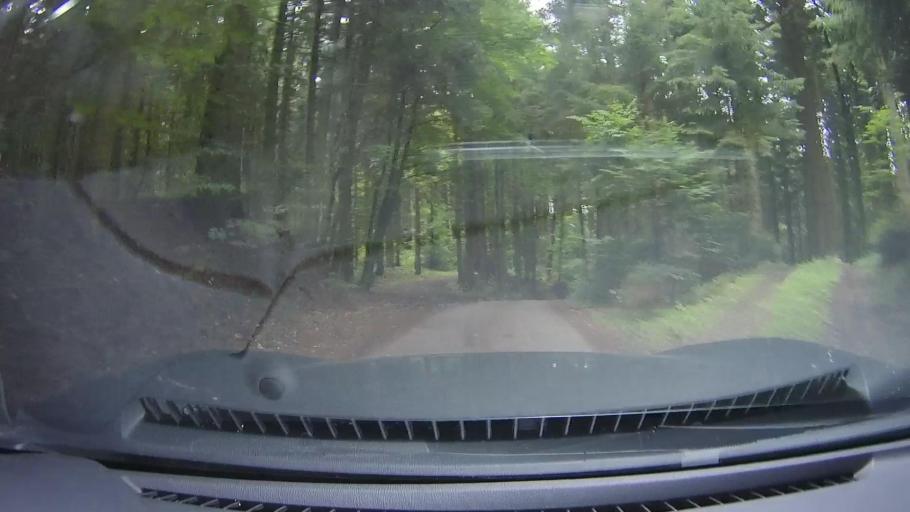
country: DE
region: Baden-Wuerttemberg
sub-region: Regierungsbezirk Stuttgart
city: Murrhardt
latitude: 48.9612
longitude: 9.5574
